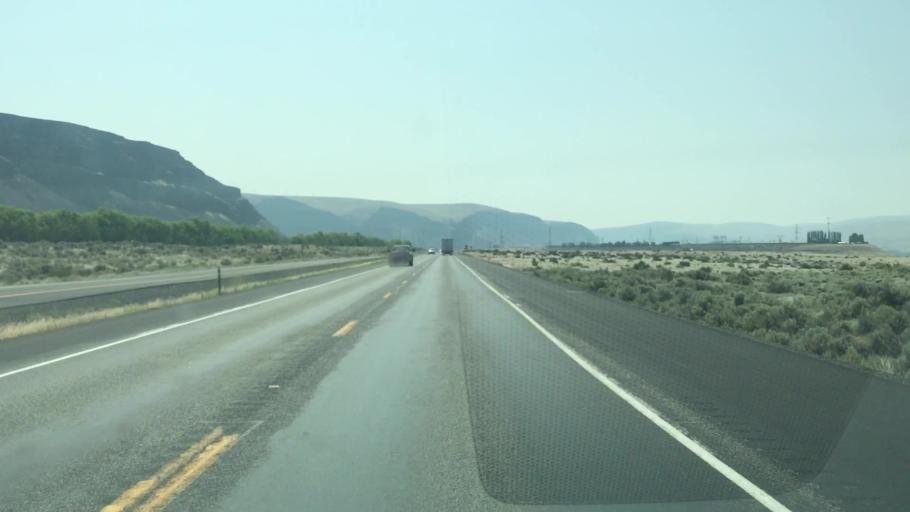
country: US
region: Washington
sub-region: Chelan County
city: South Wenatchee
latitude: 47.3194
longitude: -120.0731
